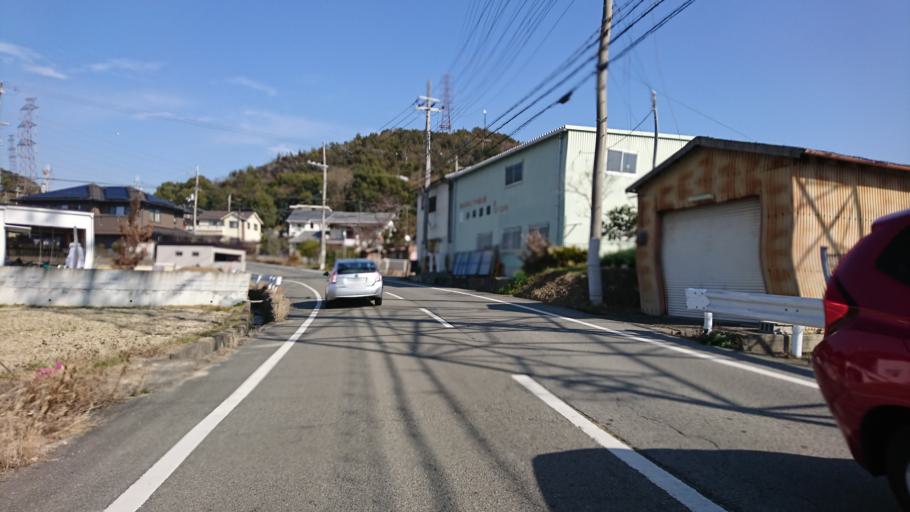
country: JP
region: Hyogo
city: Kakogawacho-honmachi
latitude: 34.7949
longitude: 134.8391
